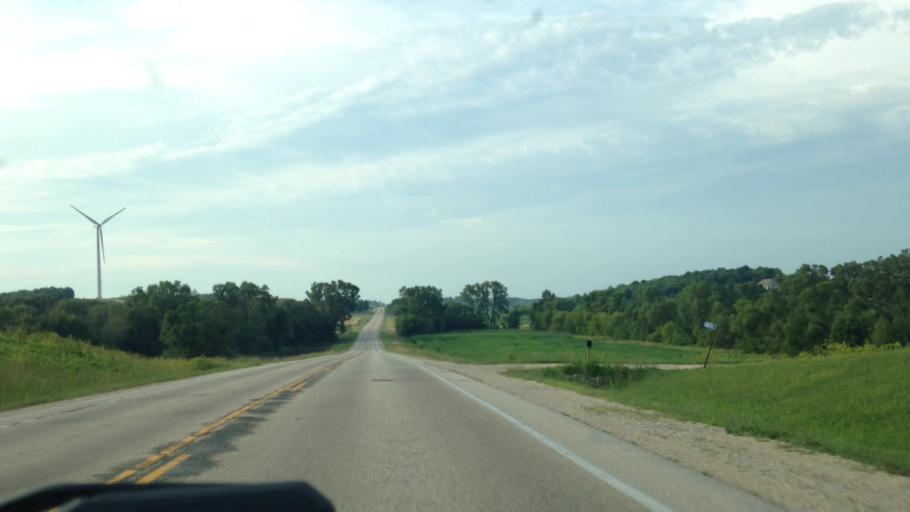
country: US
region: Wisconsin
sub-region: Dodge County
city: Theresa
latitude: 43.4369
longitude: -88.4503
